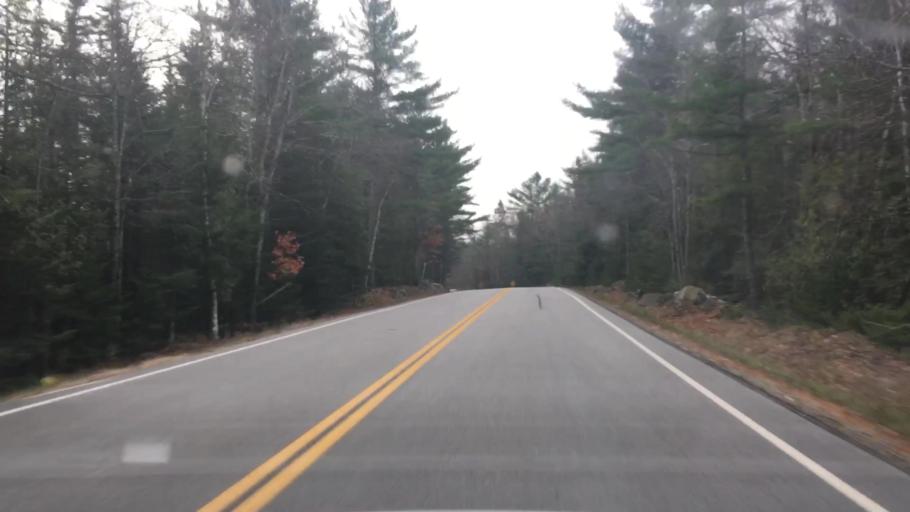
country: US
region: Maine
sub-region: Hancock County
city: Penobscot
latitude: 44.5068
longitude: -68.6557
